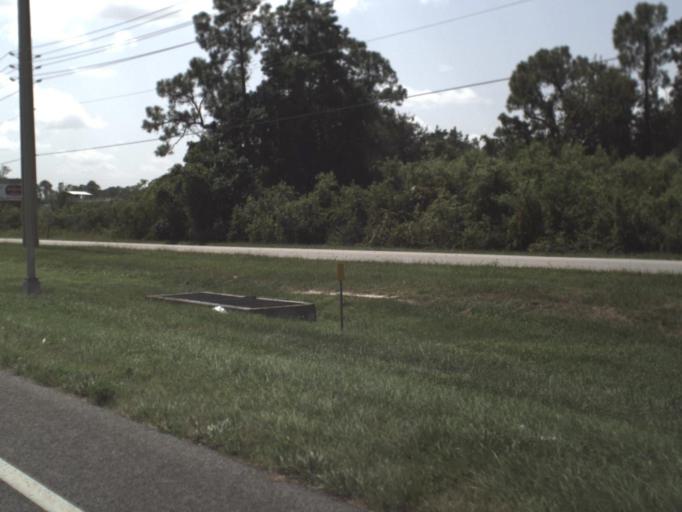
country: US
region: Florida
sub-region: Highlands County
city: Avon Park
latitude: 27.5317
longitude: -81.5014
